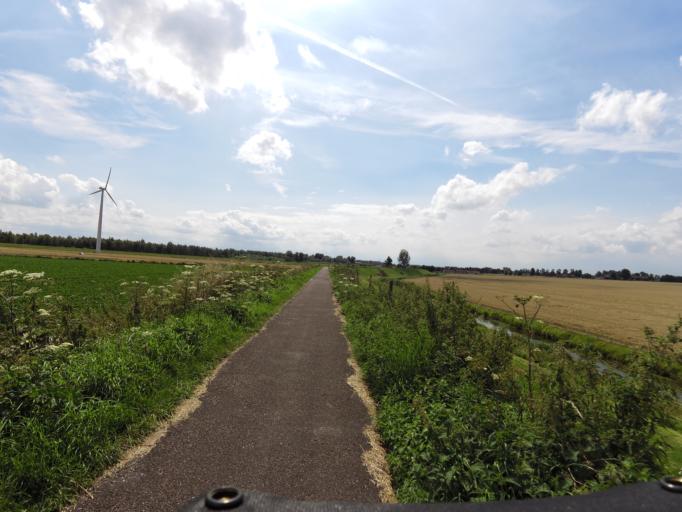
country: NL
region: South Holland
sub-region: Gemeente Strijen
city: Strijen
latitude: 51.7201
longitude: 4.5961
